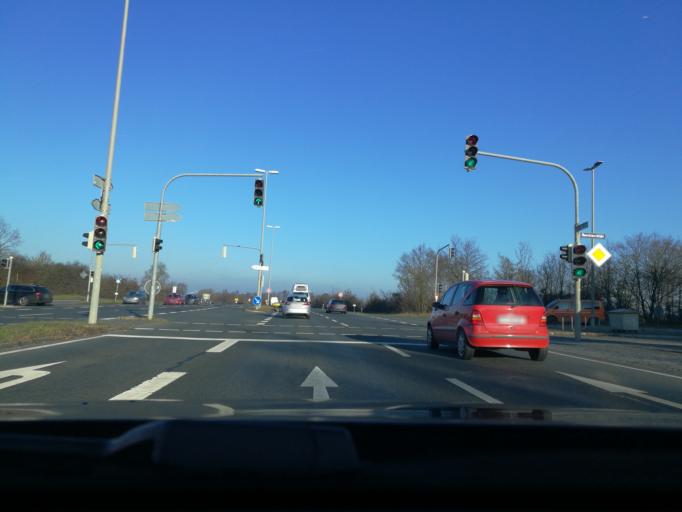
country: DE
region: Bavaria
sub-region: Regierungsbezirk Mittelfranken
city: Wetzendorf
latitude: 49.5186
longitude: 11.0334
